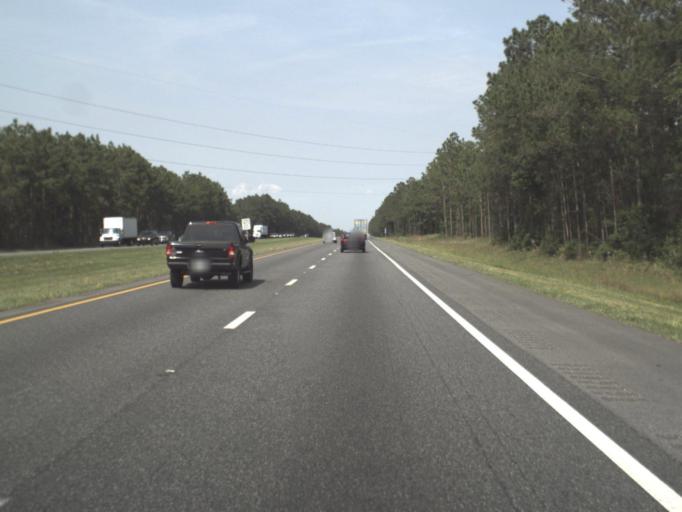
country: US
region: Florida
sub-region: Baker County
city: Macclenny
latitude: 30.2724
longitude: -82.0819
